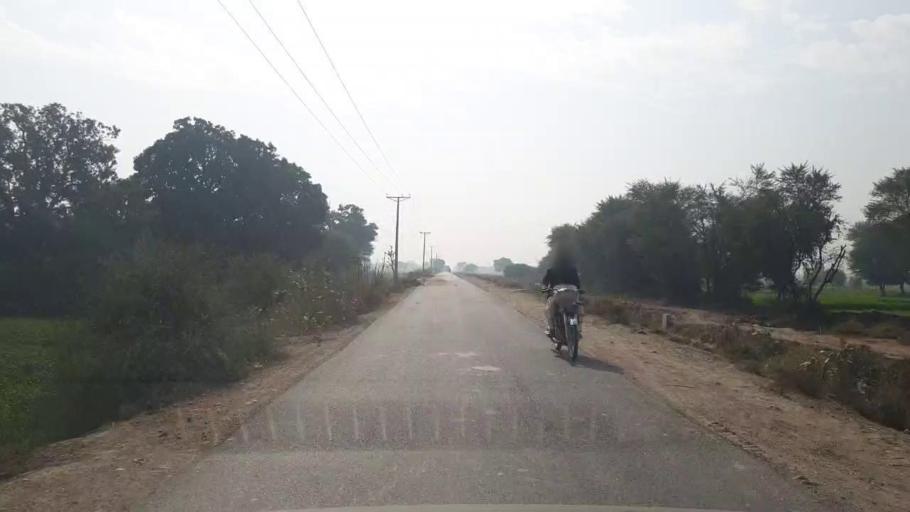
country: PK
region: Sindh
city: Hala
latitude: 25.7908
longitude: 68.4403
